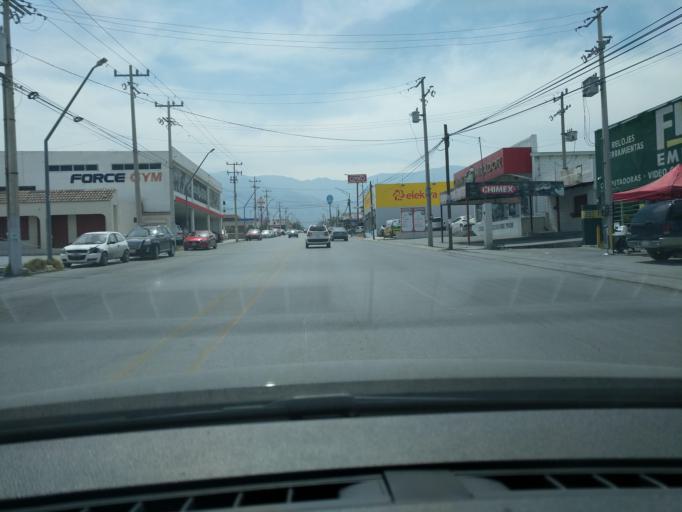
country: MX
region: Coahuila
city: Saltillo
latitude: 25.4261
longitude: -100.9458
